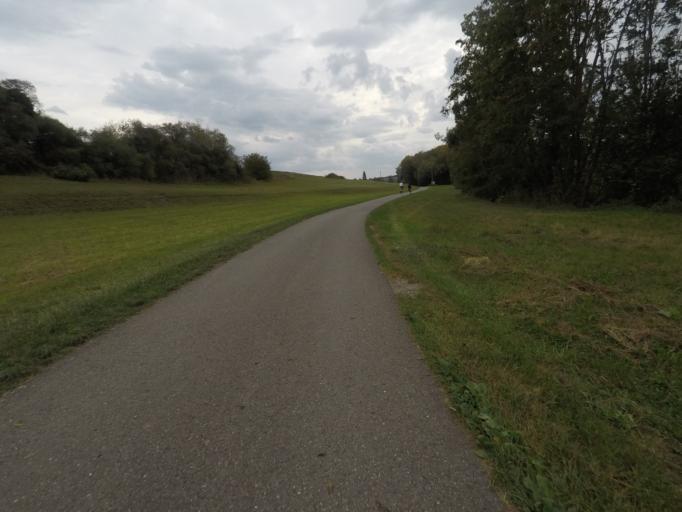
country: DE
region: Baden-Wuerttemberg
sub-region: Regierungsbezirk Stuttgart
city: Herrenberg
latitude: 48.5790
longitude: 8.8687
